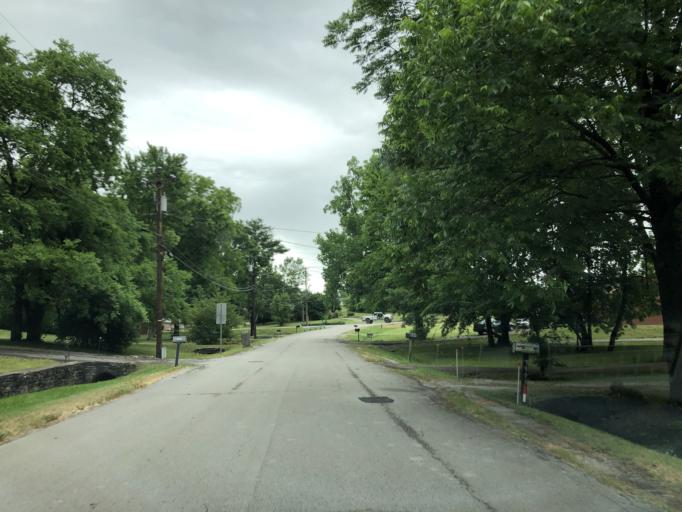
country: US
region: Tennessee
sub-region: Davidson County
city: Goodlettsville
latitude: 36.2740
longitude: -86.7653
